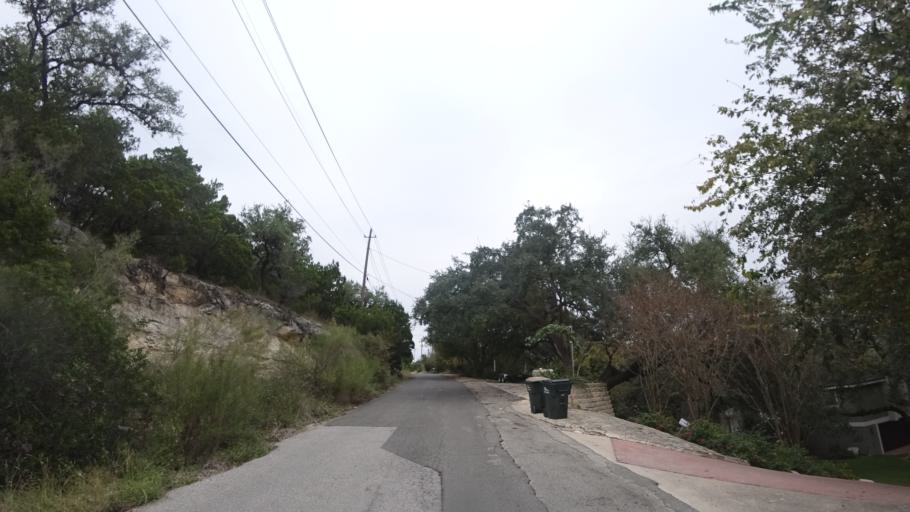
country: US
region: Texas
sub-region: Travis County
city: Hudson Bend
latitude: 30.3716
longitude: -97.9159
